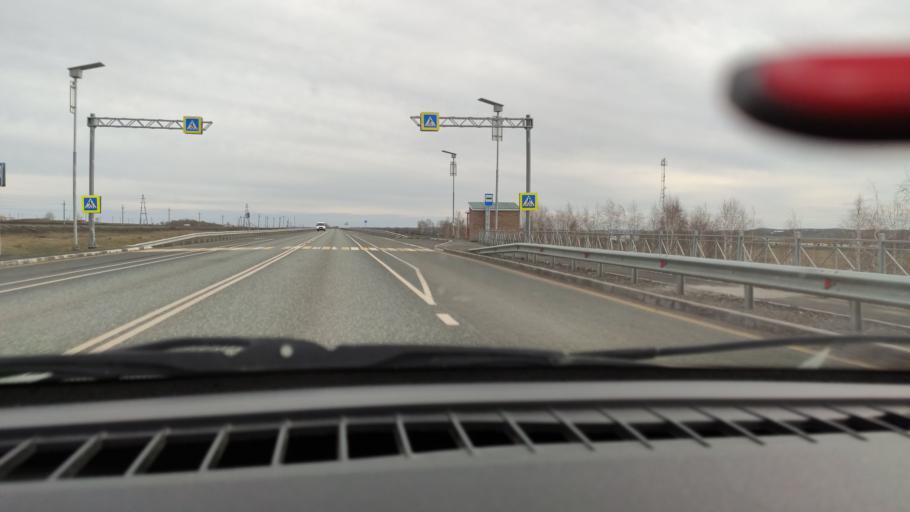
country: RU
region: Bashkortostan
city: Yermolayevo
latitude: 52.4891
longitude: 55.8289
